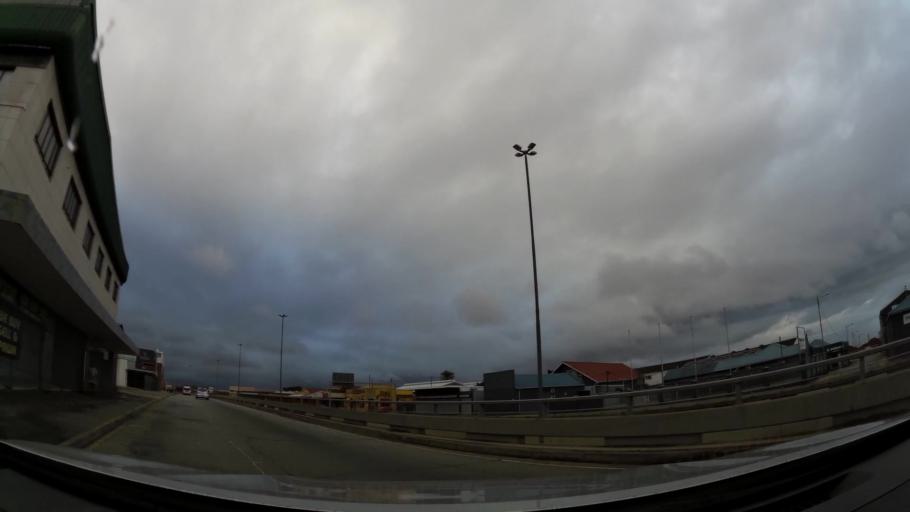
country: ZA
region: Eastern Cape
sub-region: Nelson Mandela Bay Metropolitan Municipality
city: Port Elizabeth
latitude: -33.9228
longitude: 25.5939
